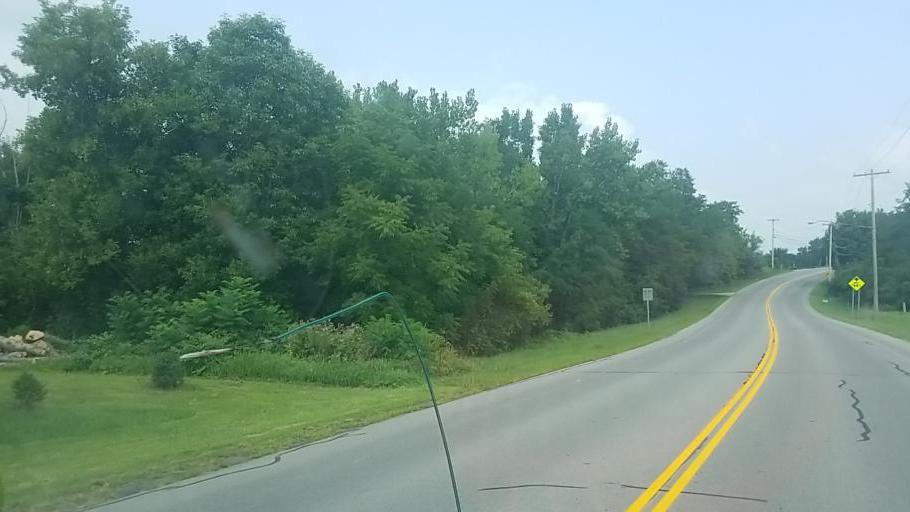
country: US
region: New York
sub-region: Montgomery County
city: Fort Plain
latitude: 42.9421
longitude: -74.6184
